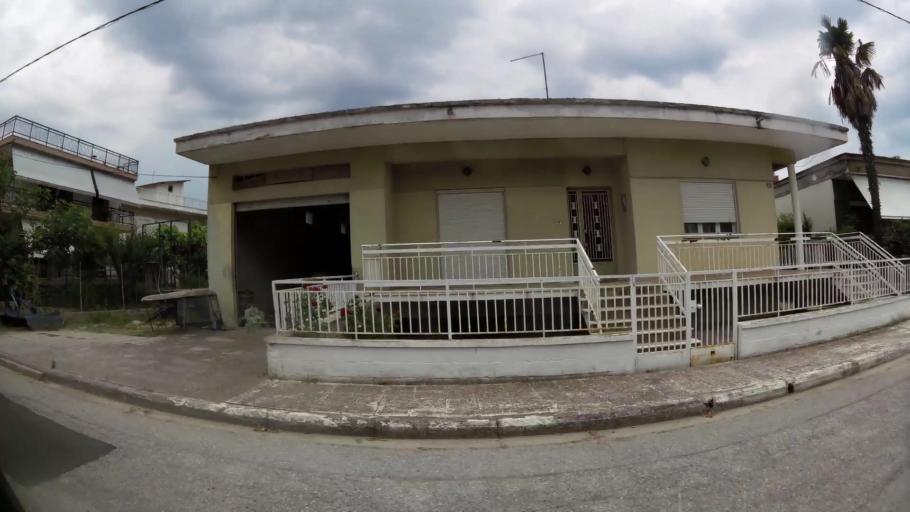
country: GR
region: Central Macedonia
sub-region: Nomos Pierias
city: Kallithea
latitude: 40.2725
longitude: 22.5799
